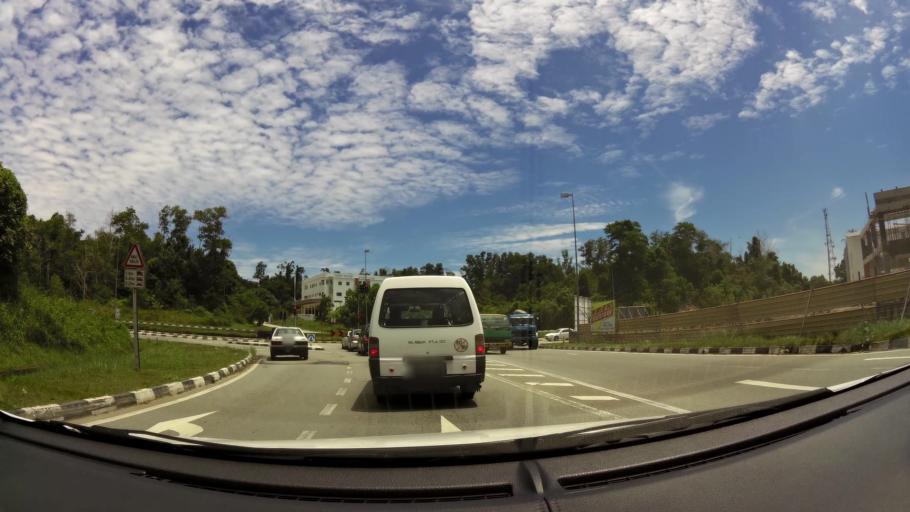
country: BN
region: Brunei and Muara
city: Bandar Seri Begawan
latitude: 4.9979
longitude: 115.0239
